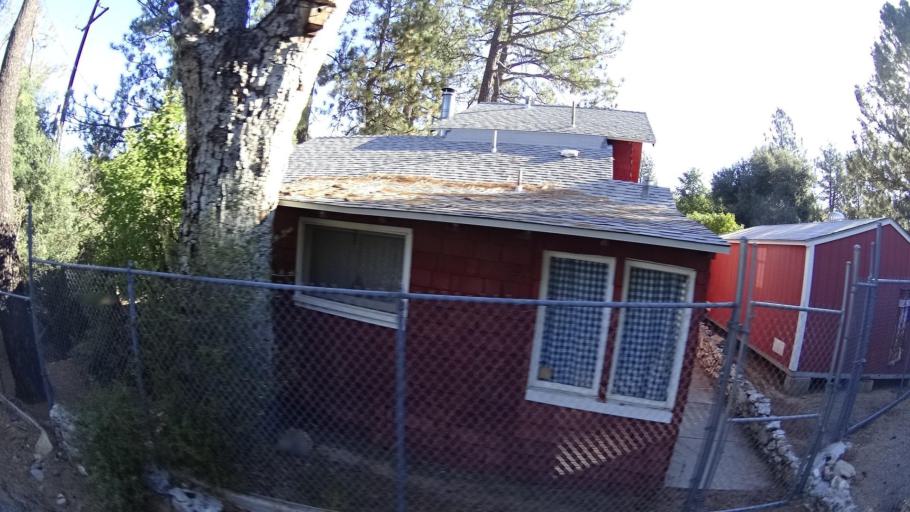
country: US
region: California
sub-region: San Diego County
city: Pine Valley
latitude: 32.8221
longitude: -116.5221
